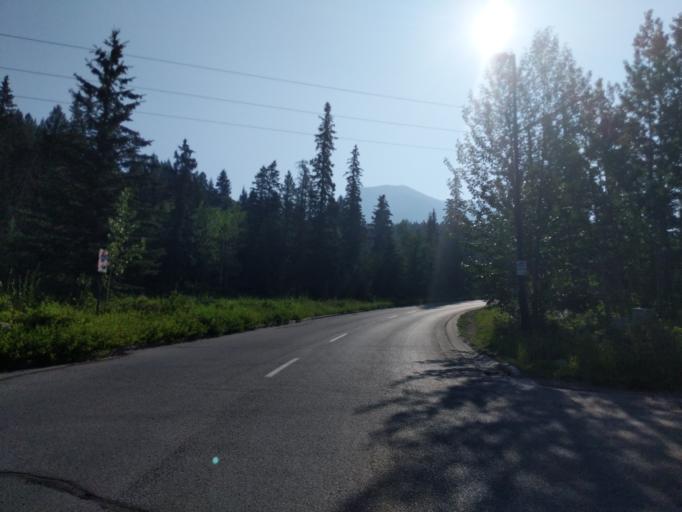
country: CA
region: Alberta
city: Canmore
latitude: 51.0940
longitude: -115.3447
